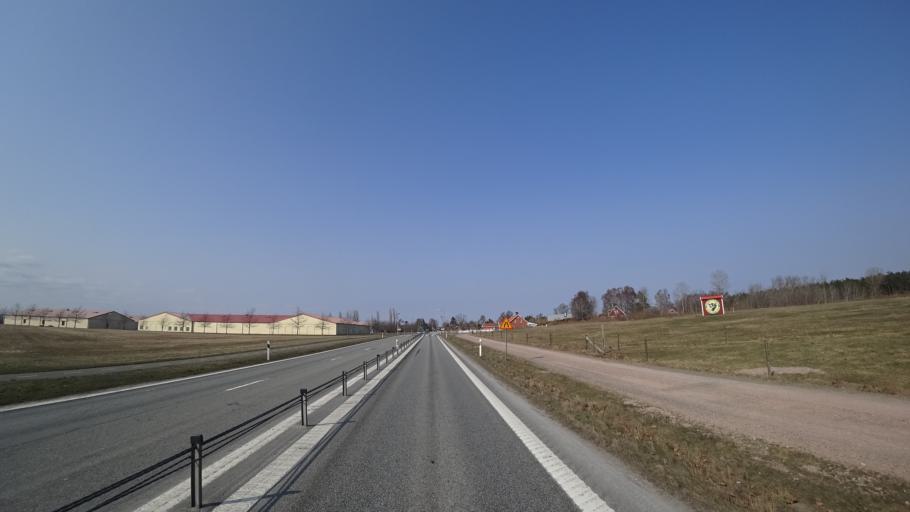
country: SE
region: Skane
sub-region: Kristianstads Kommun
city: Ahus
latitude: 55.9746
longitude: 14.2732
